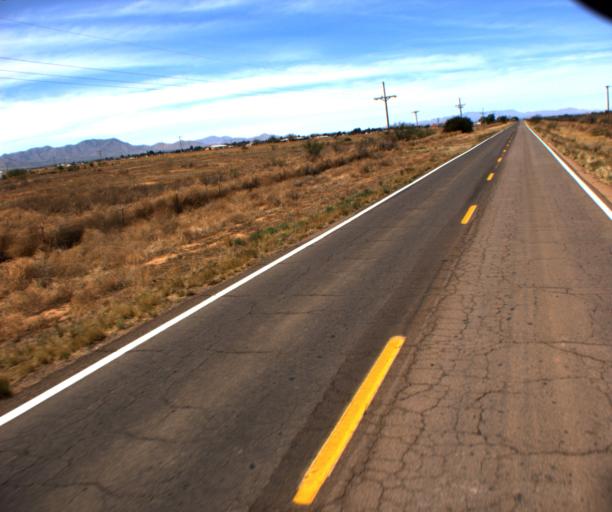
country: US
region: Arizona
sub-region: Cochise County
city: Tombstone
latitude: 31.9255
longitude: -109.8235
